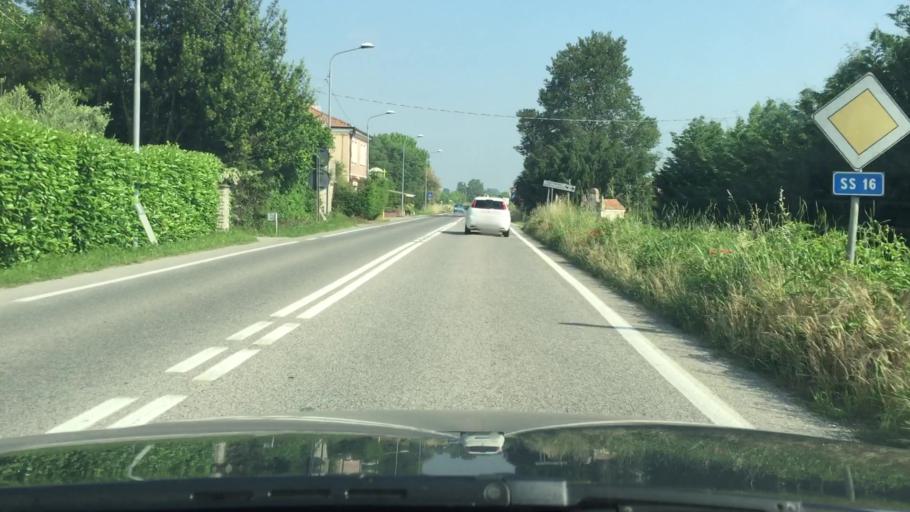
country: IT
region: Emilia-Romagna
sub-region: Provincia di Ferrara
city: Pontegradella
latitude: 44.8082
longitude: 11.6355
